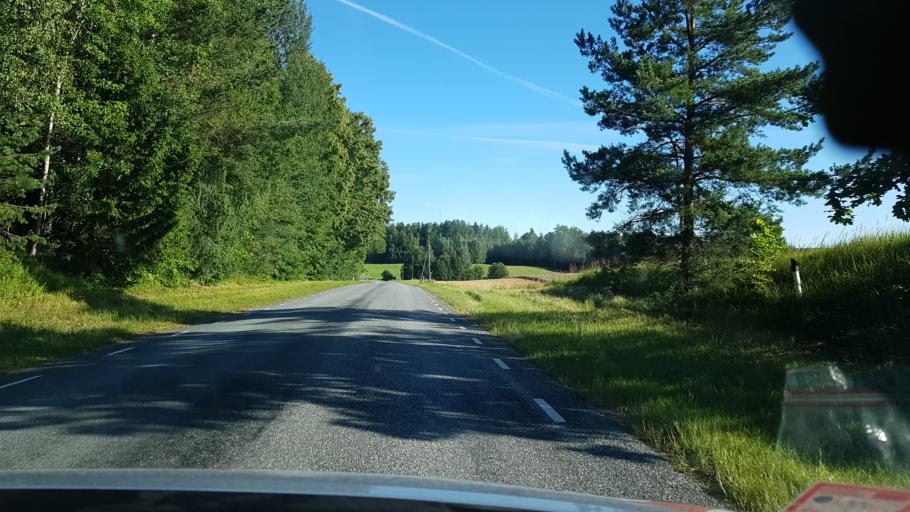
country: EE
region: Valgamaa
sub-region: Valga linn
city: Valga
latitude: 57.6616
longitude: 26.2884
